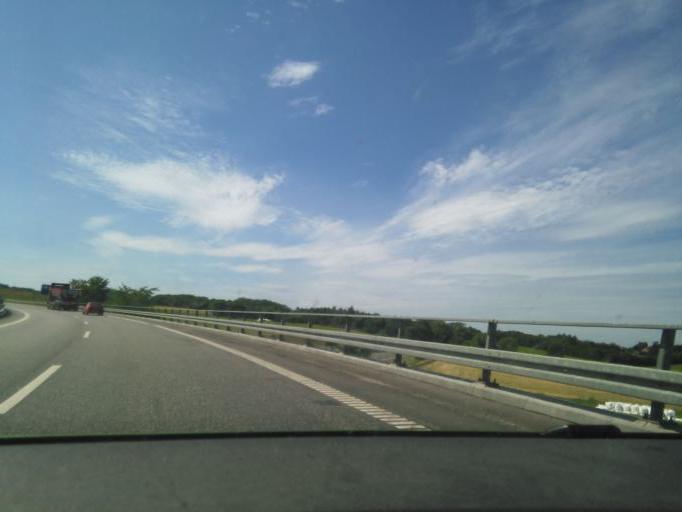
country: DK
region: Zealand
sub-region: Holbaek Kommune
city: Vipperod
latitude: 55.6511
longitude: 11.7734
